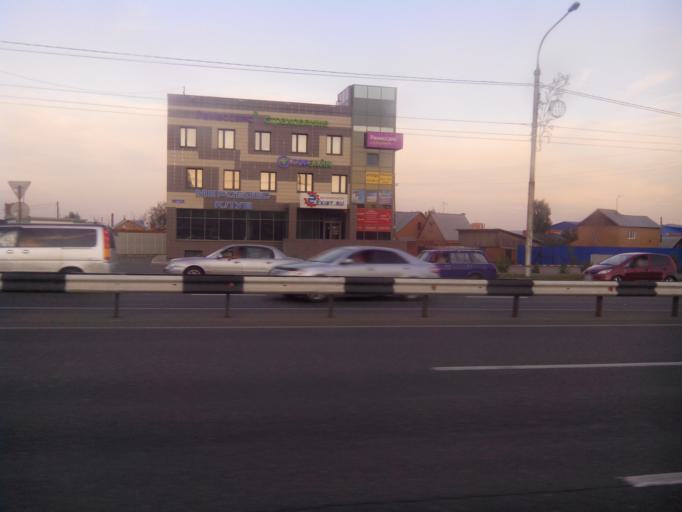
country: RU
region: Krasnoyarskiy
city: Krasnoyarsk
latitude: 56.0318
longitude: 92.8905
